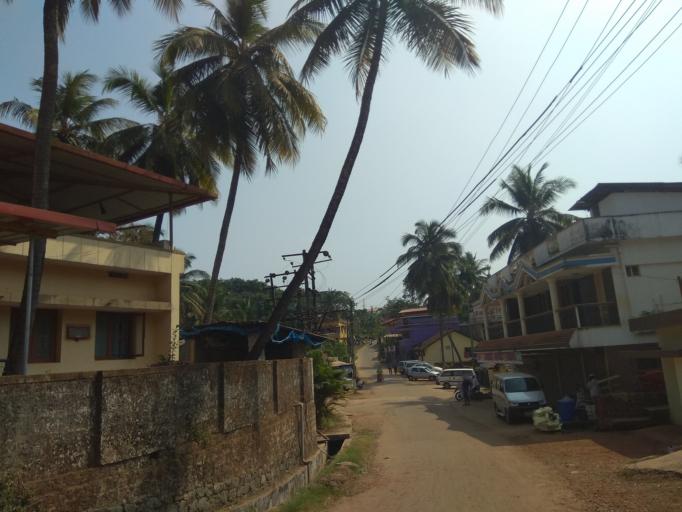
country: IN
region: Karnataka
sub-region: Dakshina Kannada
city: Mangalore
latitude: 12.9279
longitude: 74.8432
